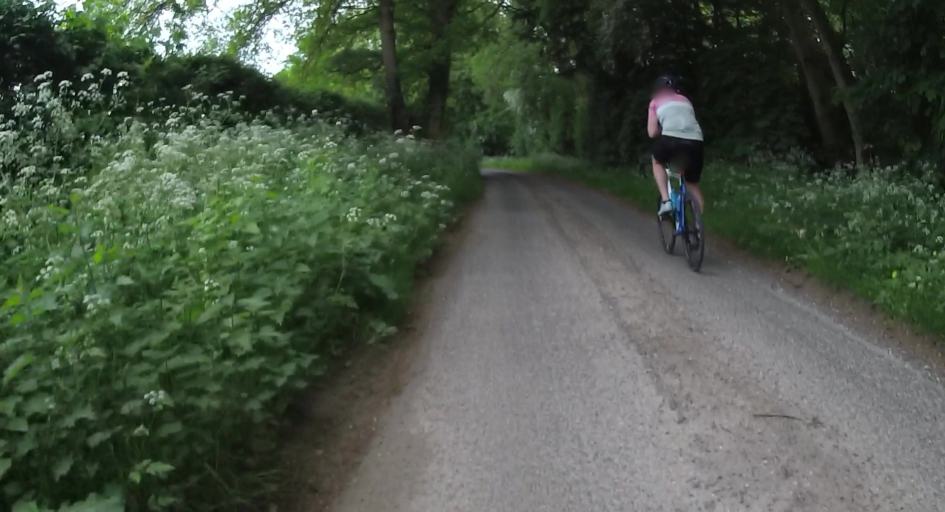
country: GB
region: England
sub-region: Hampshire
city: Overton
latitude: 51.2770
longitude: -1.2571
